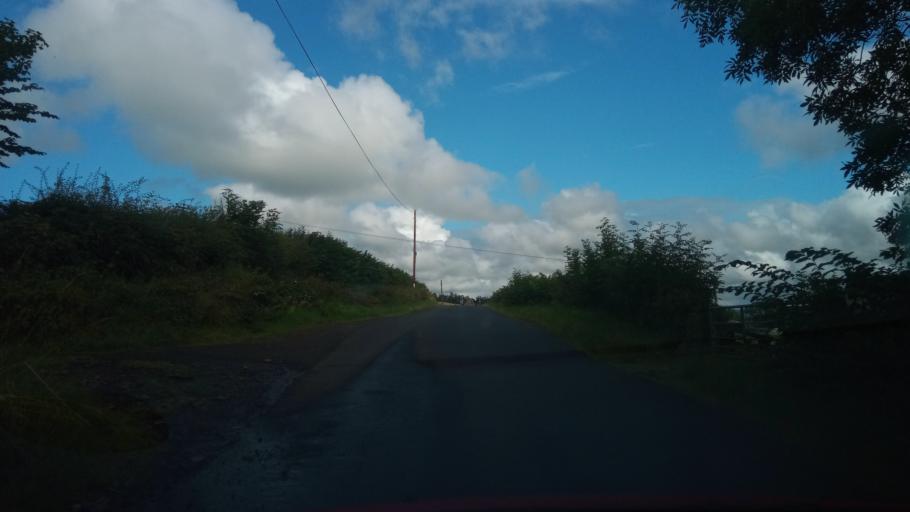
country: GB
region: Scotland
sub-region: The Scottish Borders
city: Earlston
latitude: 55.6342
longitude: -2.6903
